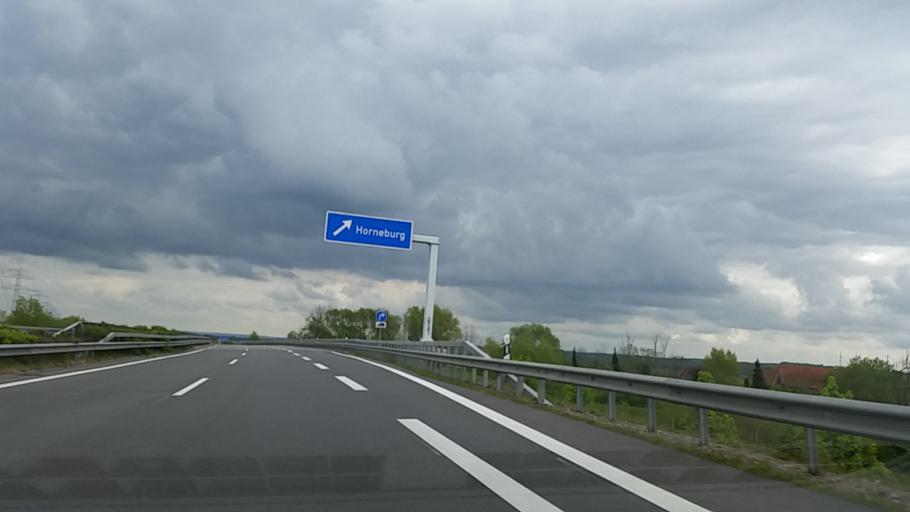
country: DE
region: Lower Saxony
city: Neuenkirchen
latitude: 53.5158
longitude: 9.5916
